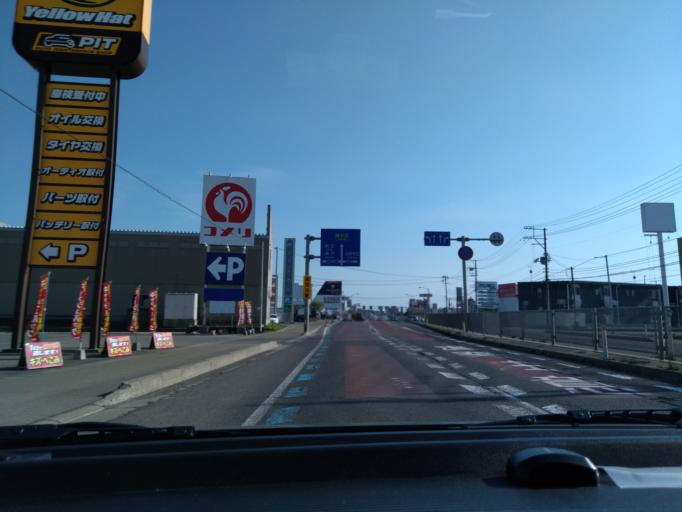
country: JP
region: Akita
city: Yokotemachi
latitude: 39.3037
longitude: 140.5574
